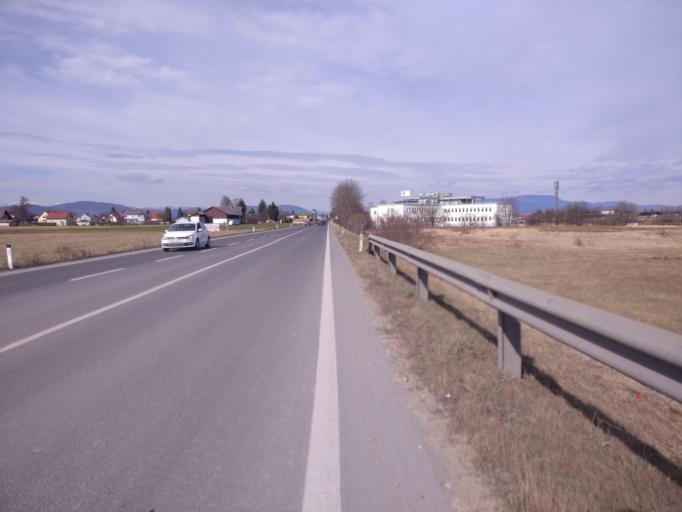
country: AT
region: Styria
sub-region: Politischer Bezirk Graz-Umgebung
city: Gossendorf
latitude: 46.9802
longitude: 15.4545
